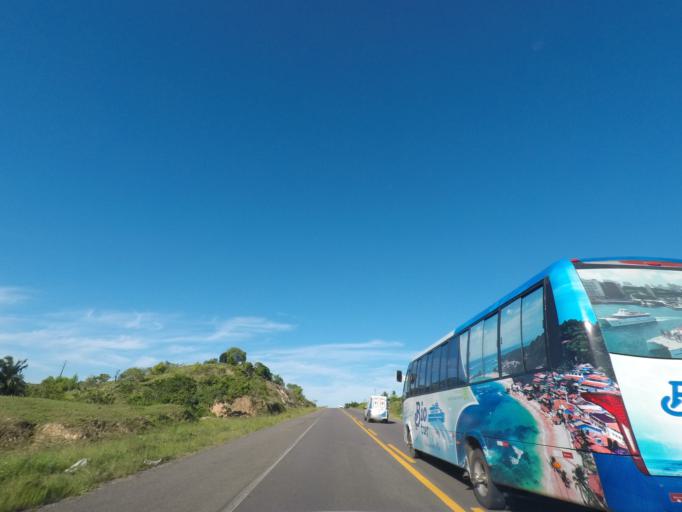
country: BR
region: Bahia
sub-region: Nazare
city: Nazare
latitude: -13.0271
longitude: -38.9909
